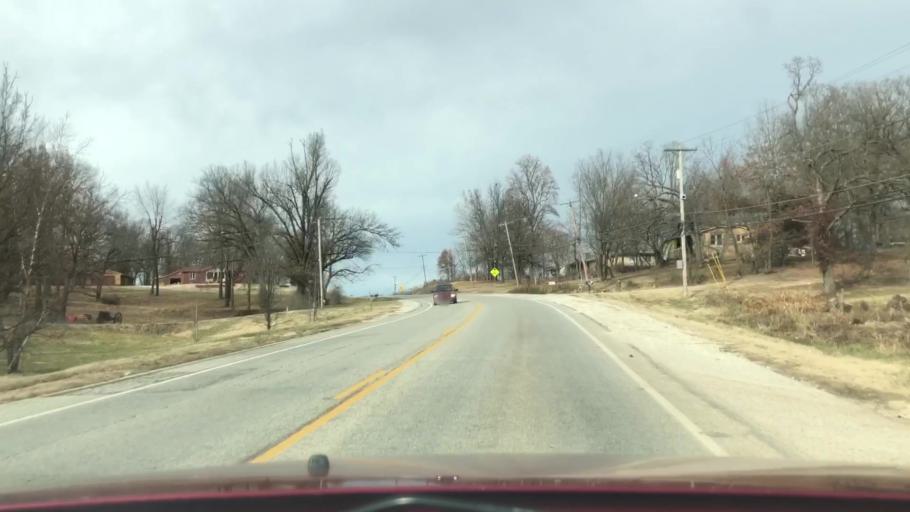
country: US
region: Missouri
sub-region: Greene County
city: Springfield
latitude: 37.2779
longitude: -93.2630
